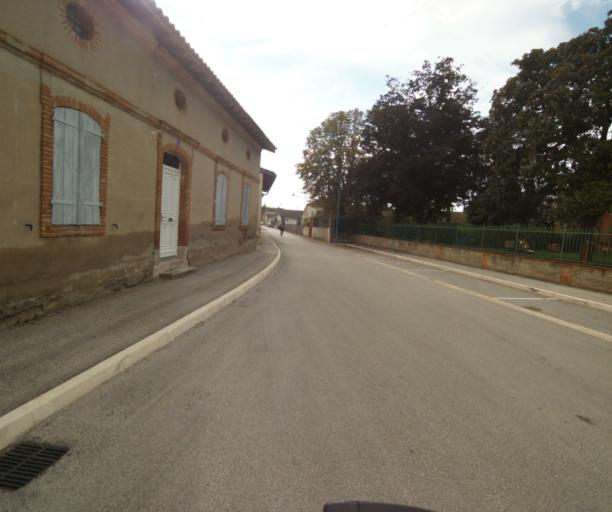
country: FR
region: Midi-Pyrenees
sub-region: Departement du Tarn-et-Garonne
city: Finhan
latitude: 43.9127
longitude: 1.2204
